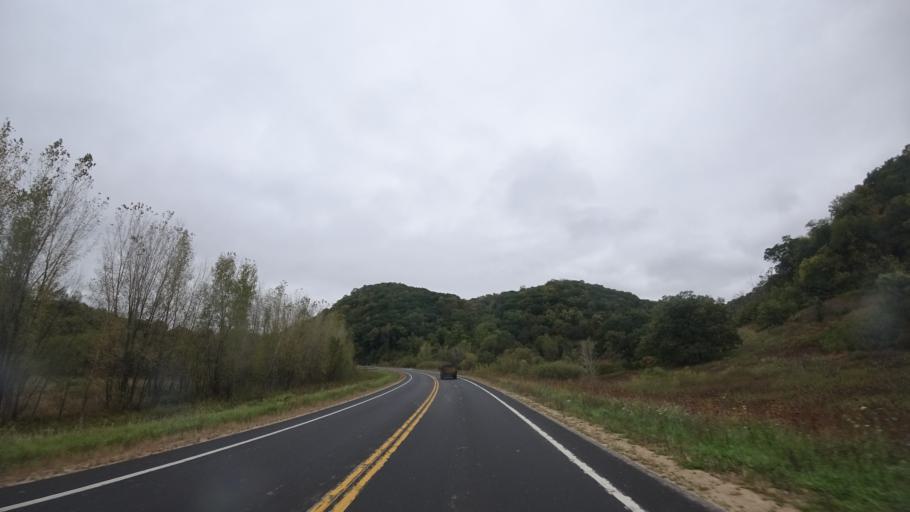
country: US
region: Wisconsin
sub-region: Grant County
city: Boscobel
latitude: 43.1453
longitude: -90.7320
